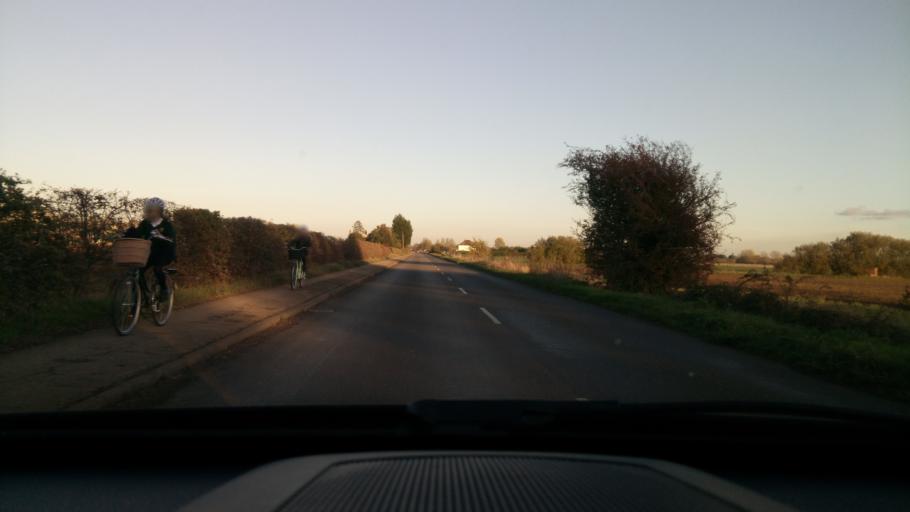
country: GB
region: England
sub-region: Peterborough
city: Helpston
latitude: 52.6365
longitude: -0.3262
